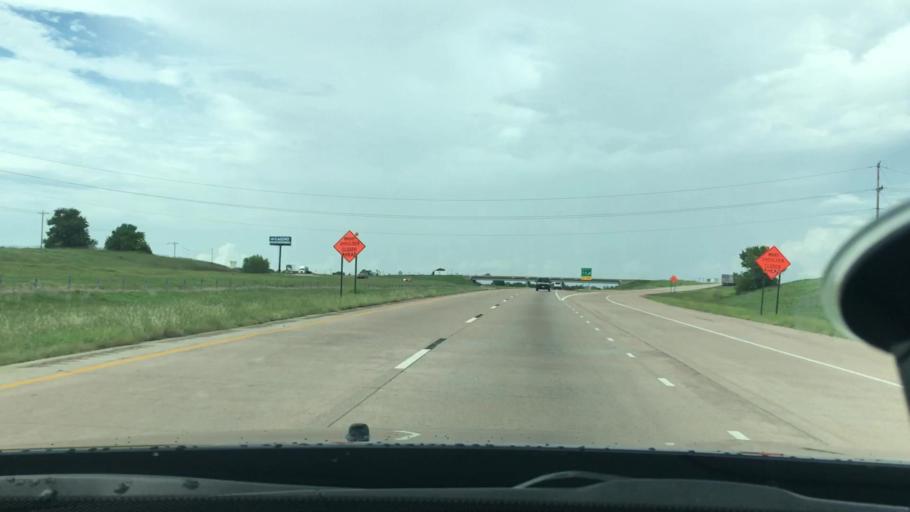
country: US
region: Oklahoma
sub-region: Garvin County
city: Pauls Valley
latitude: 34.7024
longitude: -97.2417
